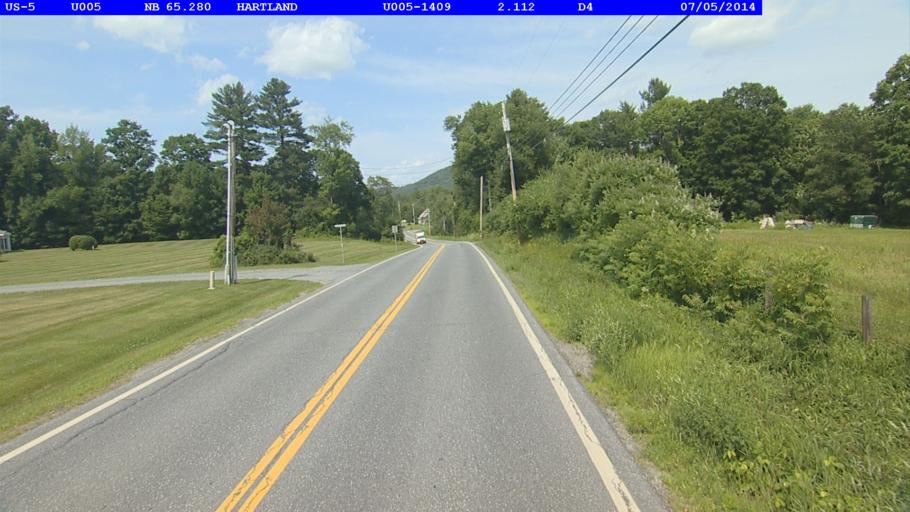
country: US
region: Vermont
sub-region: Windsor County
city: Windsor
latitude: 43.5429
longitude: -72.3896
